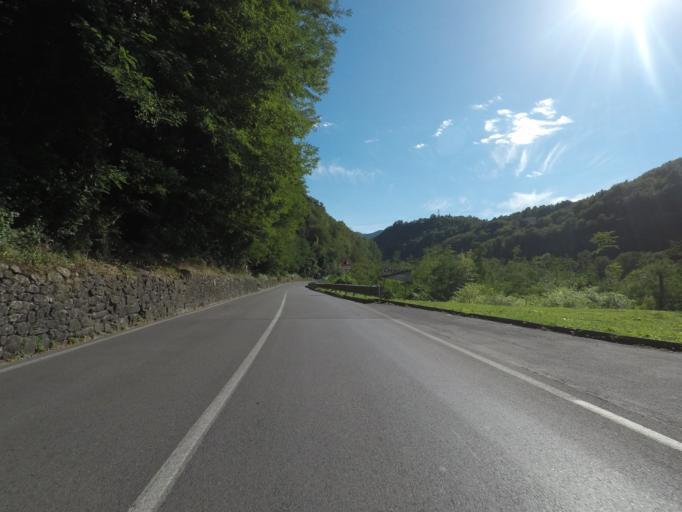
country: IT
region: Tuscany
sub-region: Provincia di Lucca
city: Bagni di Lucca
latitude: 43.9964
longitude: 10.5565
